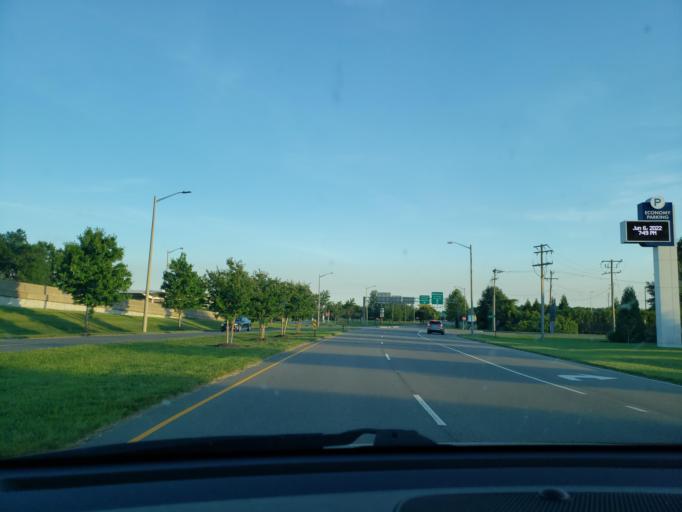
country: US
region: Virginia
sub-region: Henrico County
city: Fort Lee
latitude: 37.5114
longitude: -77.3363
